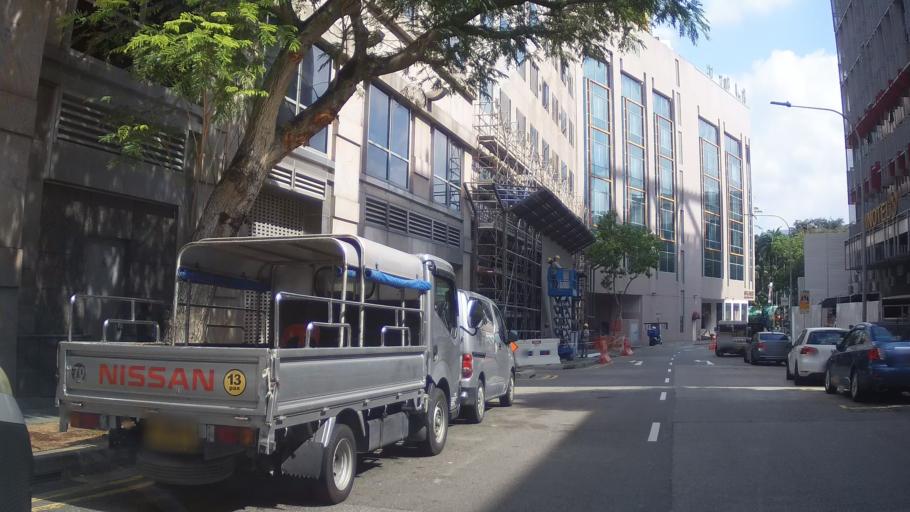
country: SG
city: Singapore
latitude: 1.2972
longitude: 103.8443
